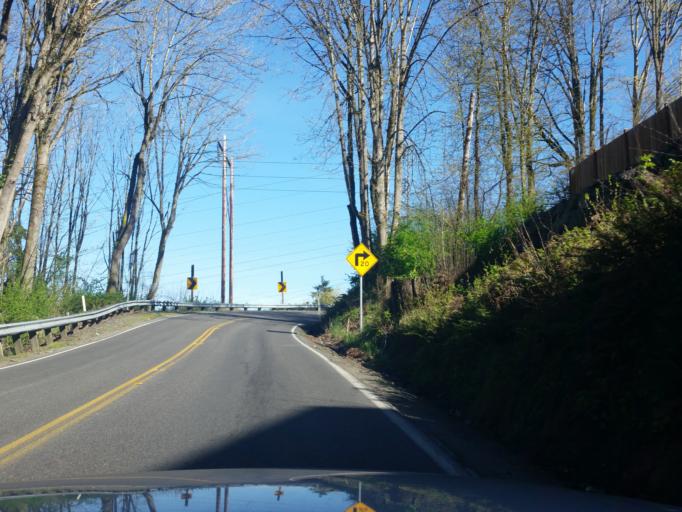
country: US
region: Washington
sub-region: Snohomish County
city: Silver Firs
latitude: 47.8907
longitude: -122.1479
